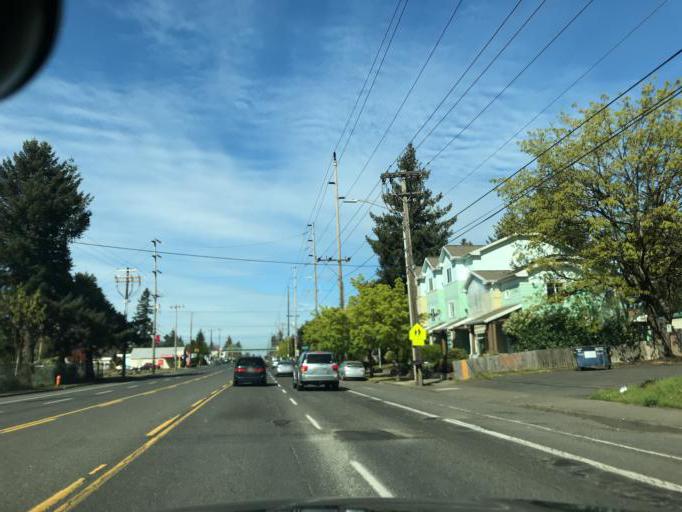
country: US
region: Oregon
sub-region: Multnomah County
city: Lents
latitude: 45.5041
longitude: -122.5195
